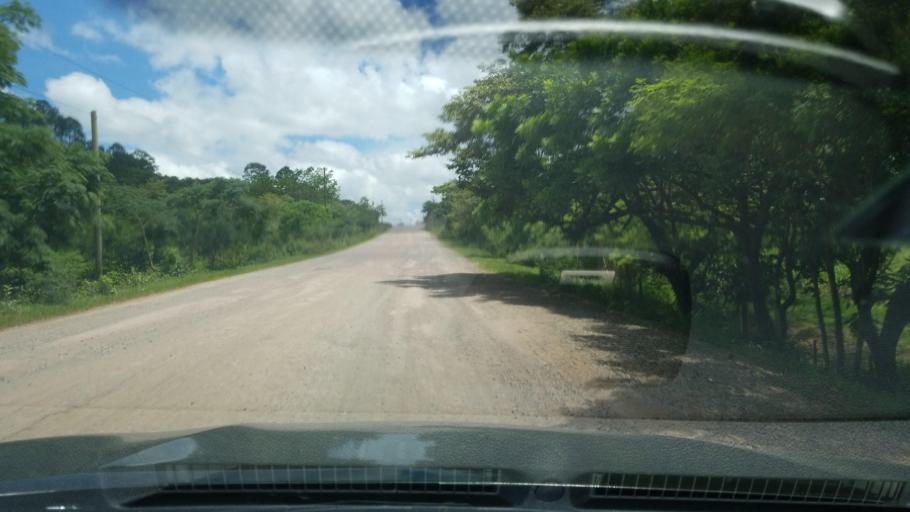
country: HN
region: Francisco Morazan
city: Talanga
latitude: 14.3834
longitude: -87.0695
